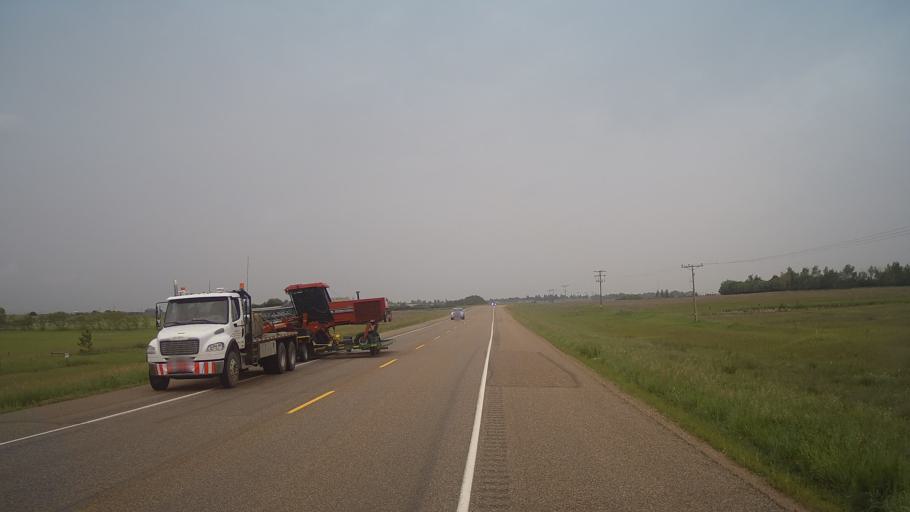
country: CA
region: Saskatchewan
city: Biggar
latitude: 52.0563
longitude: -107.9406
